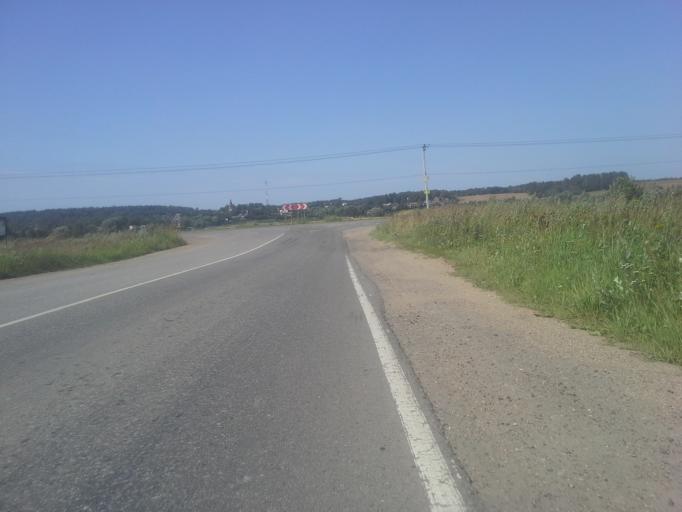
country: RU
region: Moskovskaya
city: Karinskoye
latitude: 55.6493
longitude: 36.6414
